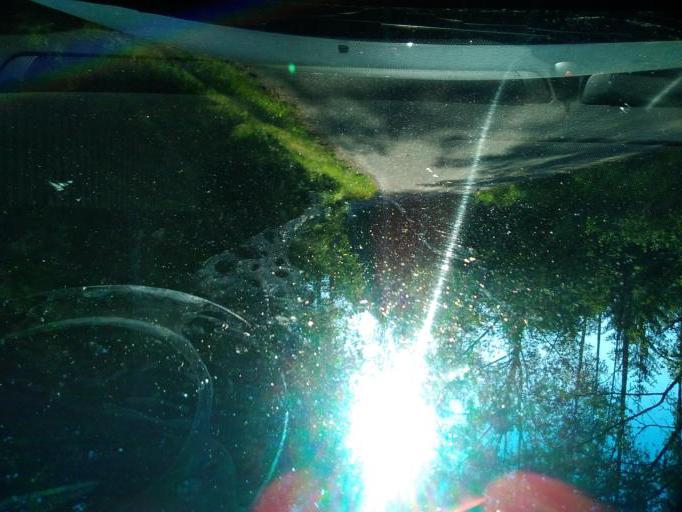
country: FI
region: Haeme
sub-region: Forssa
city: Tammela
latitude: 60.7737
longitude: 23.8153
